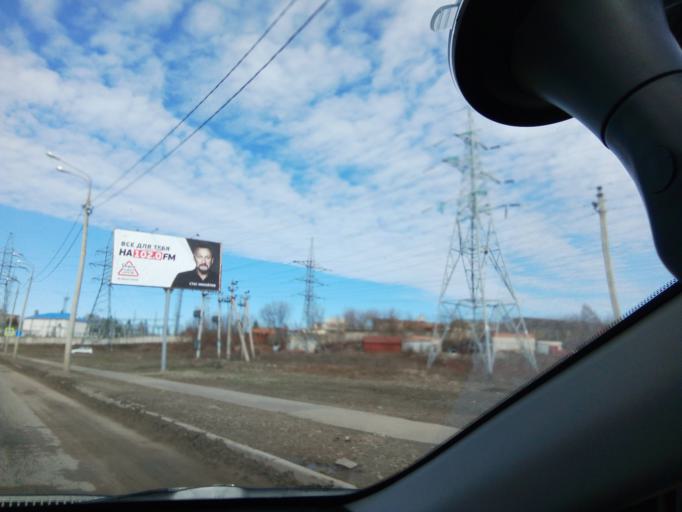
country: RU
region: Chuvashia
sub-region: Cheboksarskiy Rayon
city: Cheboksary
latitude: 56.1088
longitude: 47.2460
